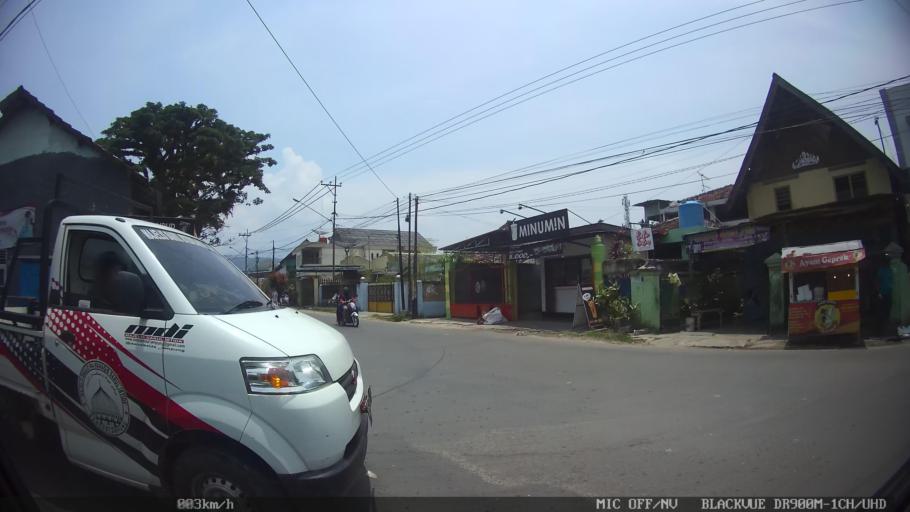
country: ID
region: Lampung
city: Bandarlampung
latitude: -5.4513
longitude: 105.2591
